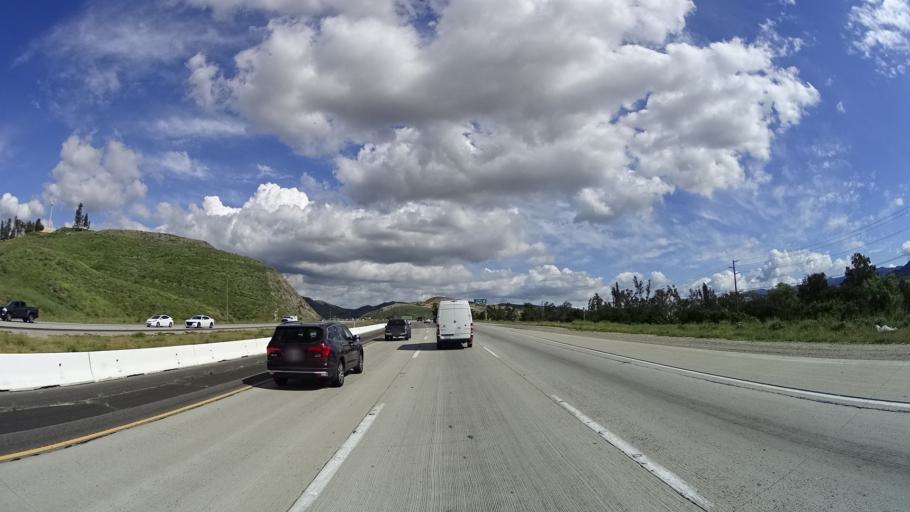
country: US
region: California
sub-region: Riverside County
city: Lake Elsinore
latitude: 33.7311
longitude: -117.4008
